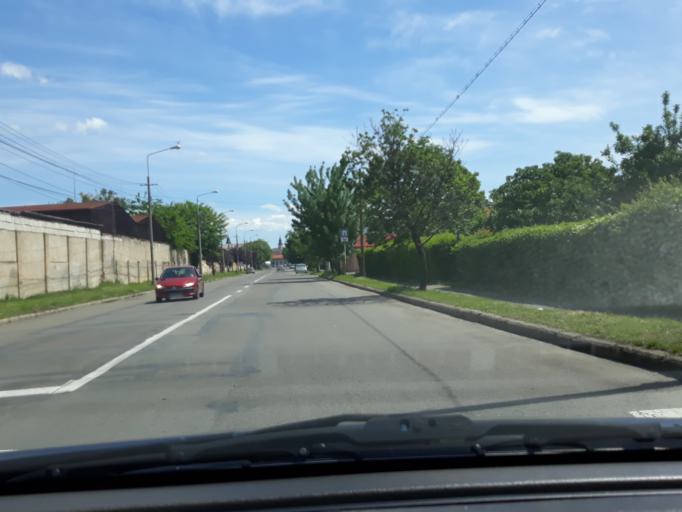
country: RO
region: Bihor
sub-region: Comuna Biharea
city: Oradea
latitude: 47.0509
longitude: 21.9122
